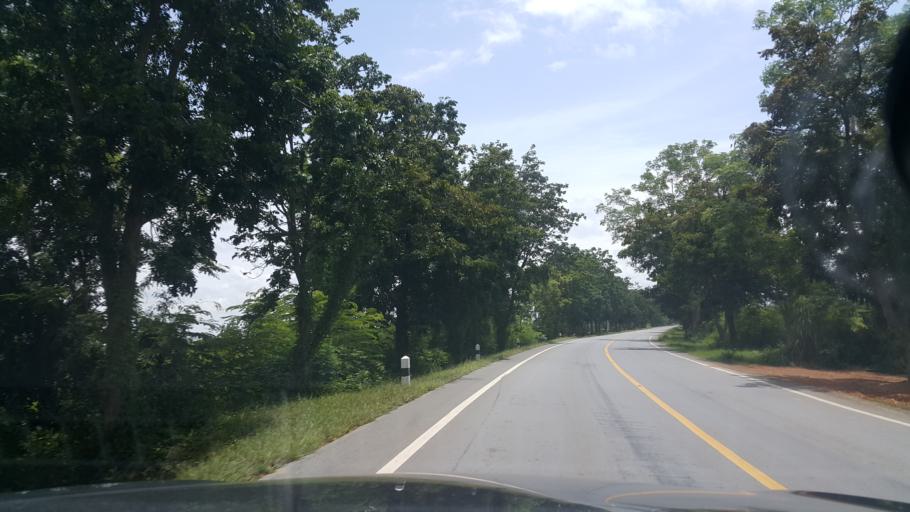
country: TH
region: Sukhothai
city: Sawankhalok
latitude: 17.3410
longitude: 99.7429
